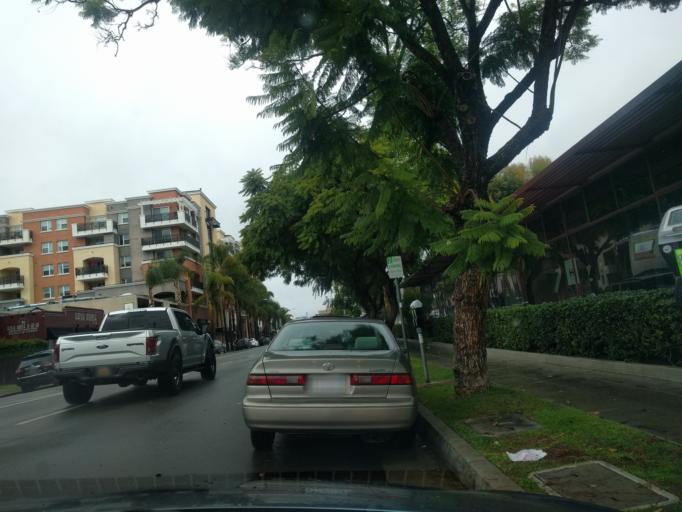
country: US
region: California
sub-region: San Diego County
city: San Diego
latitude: 32.7436
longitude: -117.1603
